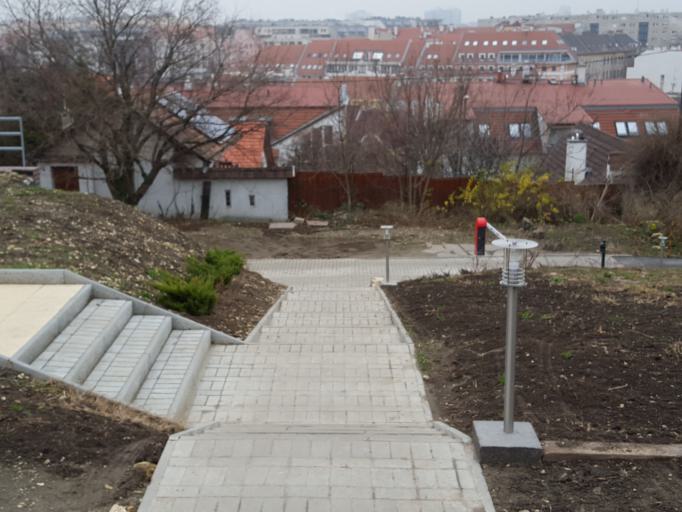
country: HU
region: Budapest
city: Budapest III. keruelet
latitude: 47.5307
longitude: 19.0355
